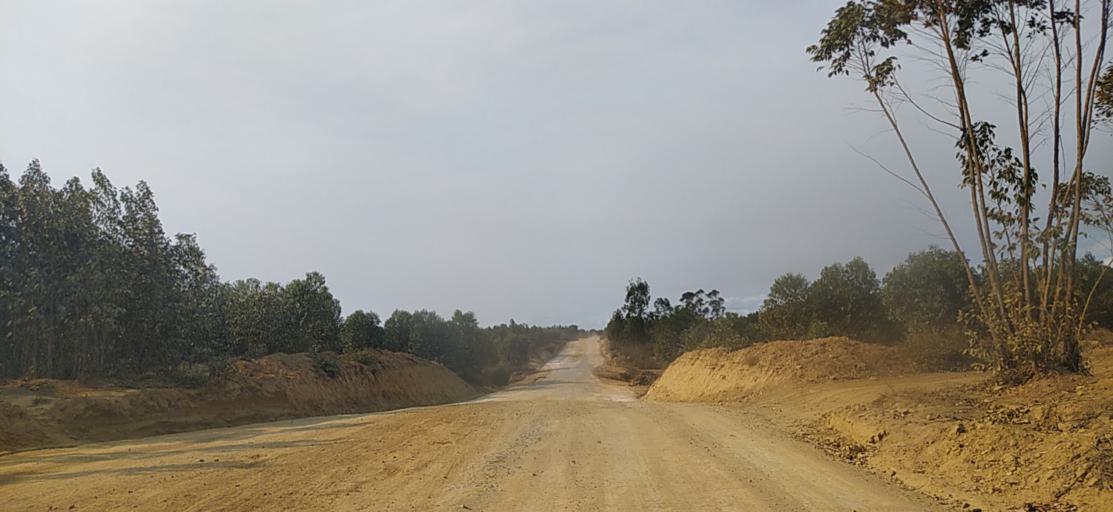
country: MG
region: Alaotra Mangoro
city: Moramanga
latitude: -18.6598
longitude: 48.2740
